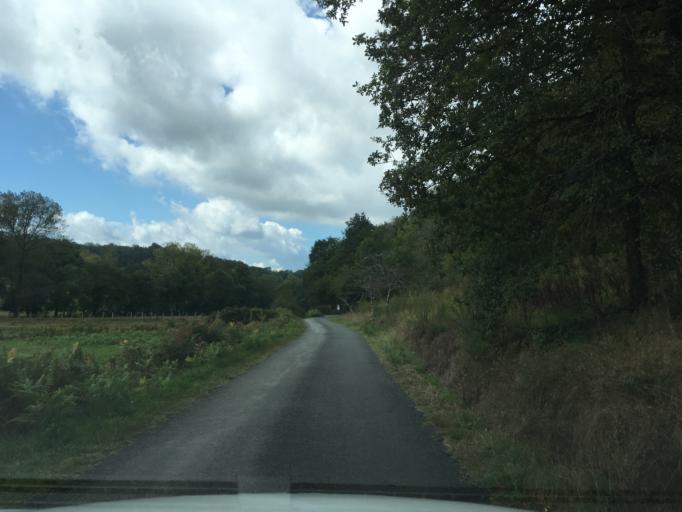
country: FR
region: Limousin
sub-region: Departement de la Correze
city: Brive-la-Gaillarde
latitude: 45.1217
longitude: 1.5462
